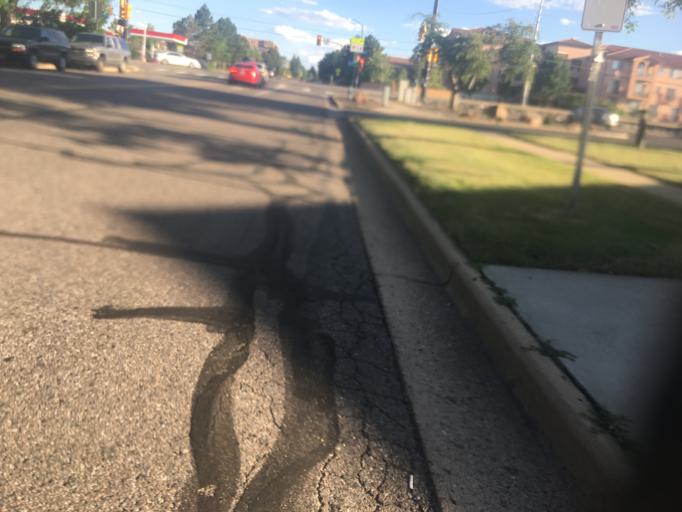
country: US
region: Colorado
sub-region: Boulder County
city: Boulder
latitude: 40.0007
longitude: -105.2366
